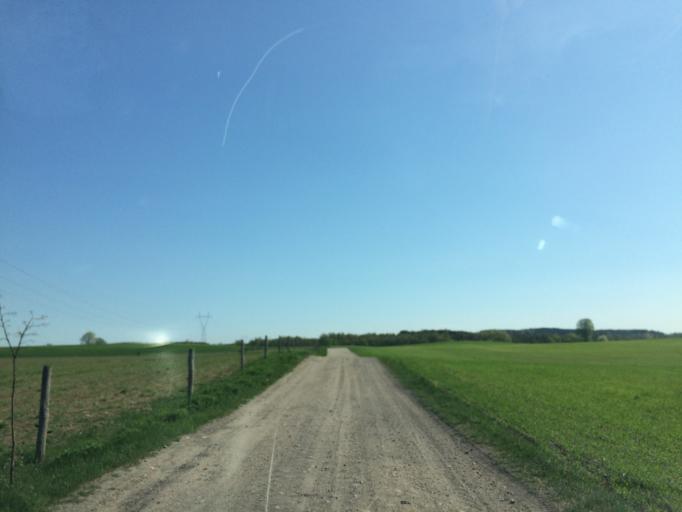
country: PL
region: Warmian-Masurian Voivodeship
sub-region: Powiat dzialdowski
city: Rybno
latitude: 53.4223
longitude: 19.9141
